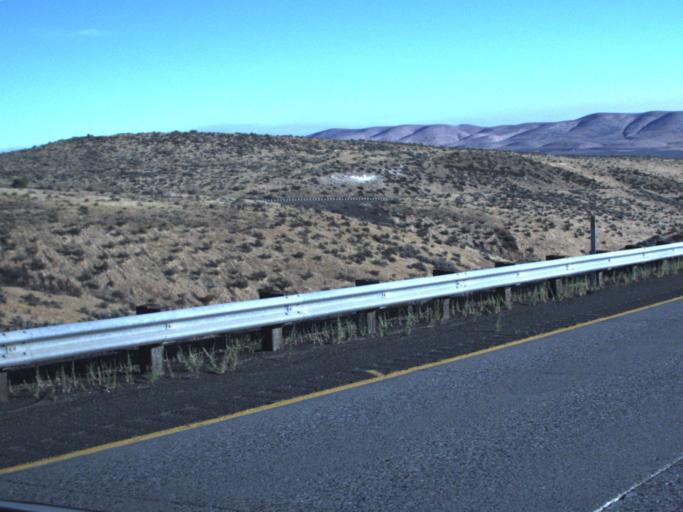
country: US
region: Washington
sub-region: Yakima County
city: Terrace Heights
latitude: 46.7754
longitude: -120.3730
